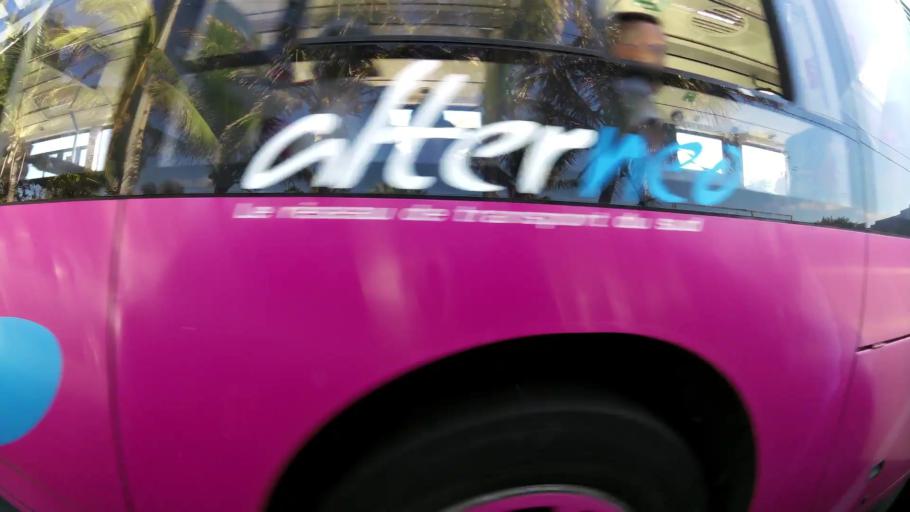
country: RE
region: Reunion
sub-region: Reunion
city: Saint-Pierre
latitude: -21.3428
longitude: 55.4683
